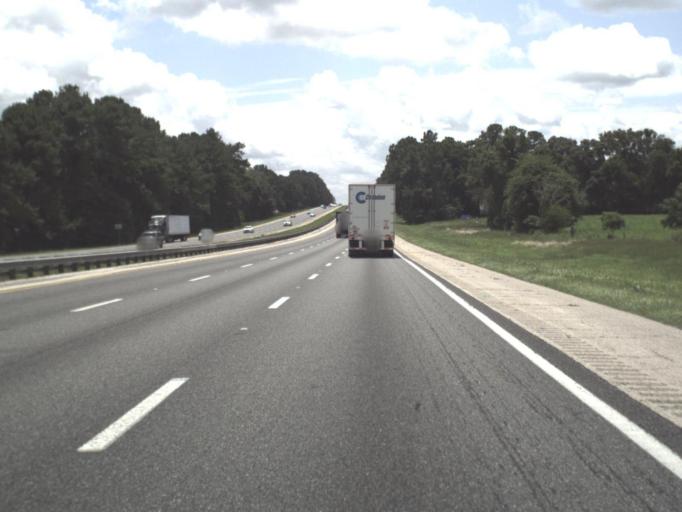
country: US
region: Florida
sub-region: Alachua County
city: High Springs
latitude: 29.8262
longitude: -82.5211
